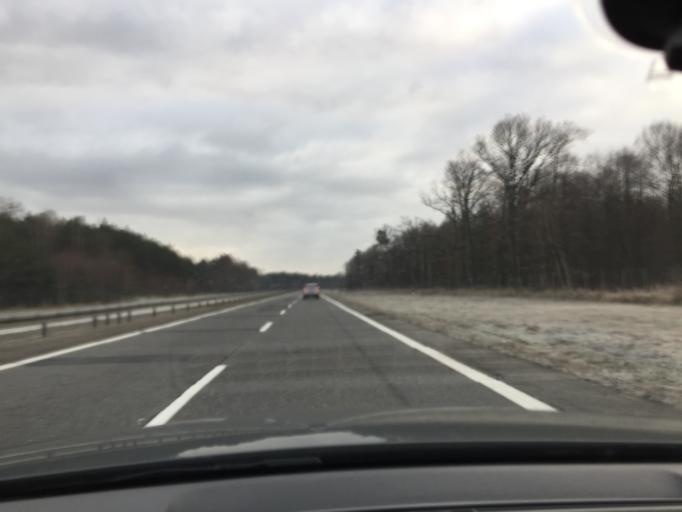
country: PL
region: Lubusz
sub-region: Powiat zarski
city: Lipinki Luzyckie
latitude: 51.6097
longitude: 14.9693
